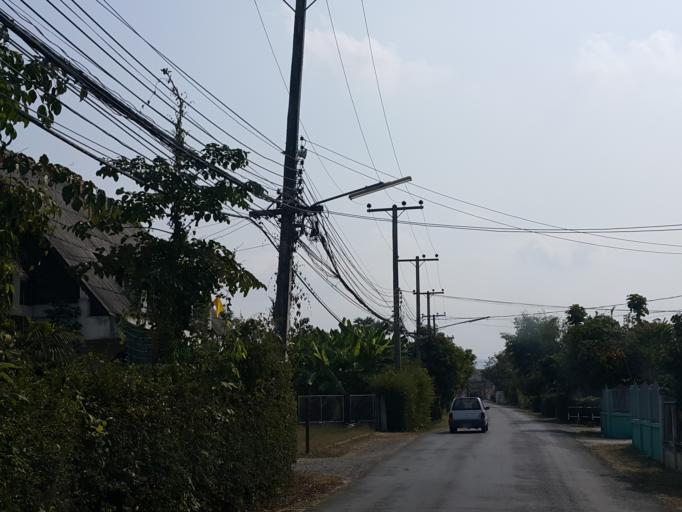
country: TH
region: Chiang Mai
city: San Kamphaeng
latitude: 18.8109
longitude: 99.1396
